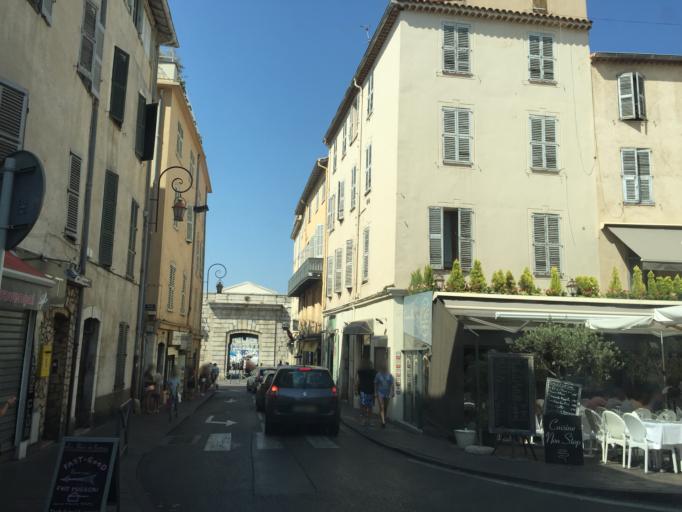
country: FR
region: Provence-Alpes-Cote d'Azur
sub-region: Departement des Alpes-Maritimes
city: Antibes
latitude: 43.5825
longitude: 7.1280
